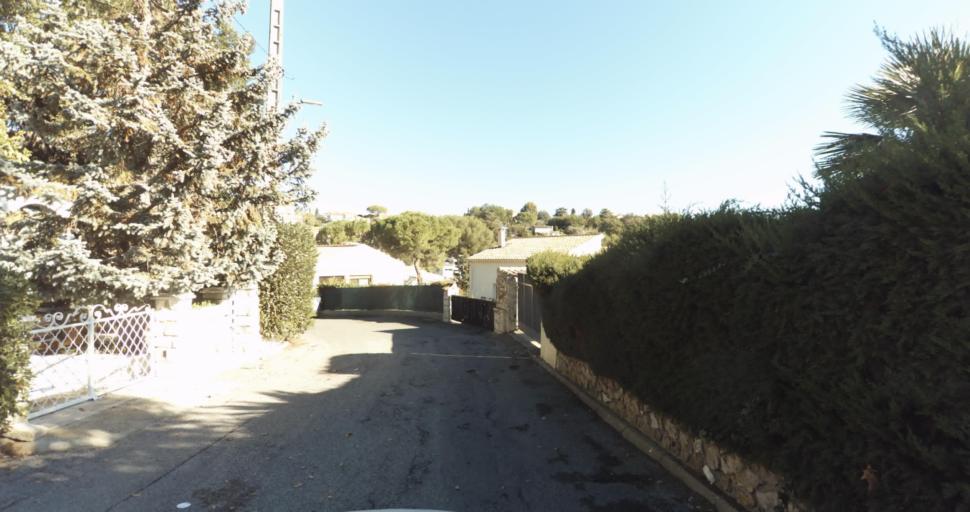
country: FR
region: Provence-Alpes-Cote d'Azur
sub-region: Departement des Alpes-Maritimes
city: Vence
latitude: 43.7181
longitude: 7.1040
